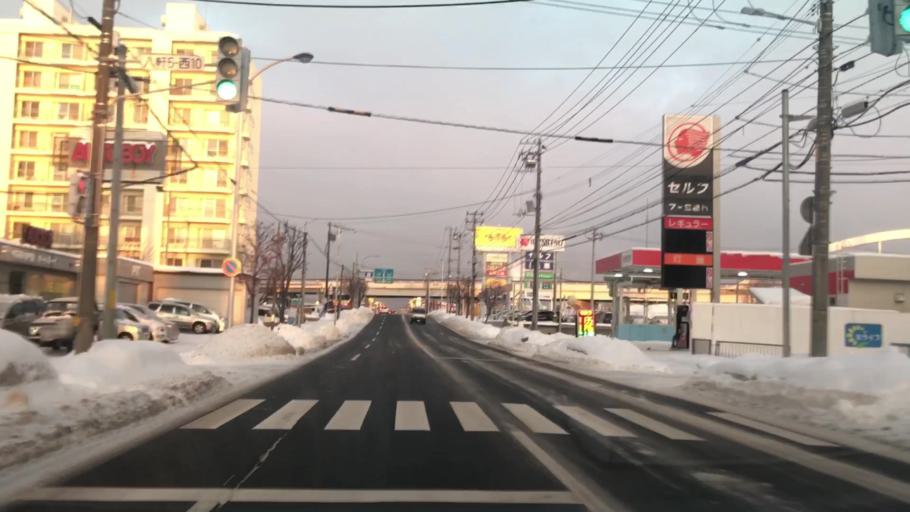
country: JP
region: Hokkaido
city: Sapporo
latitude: 43.0957
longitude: 141.3003
